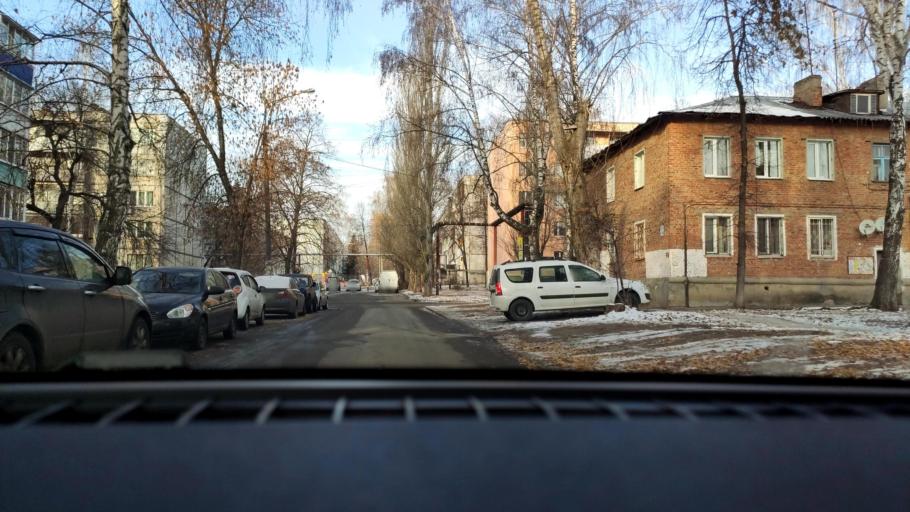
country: RU
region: Samara
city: Petra-Dubrava
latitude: 53.3018
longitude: 50.2713
